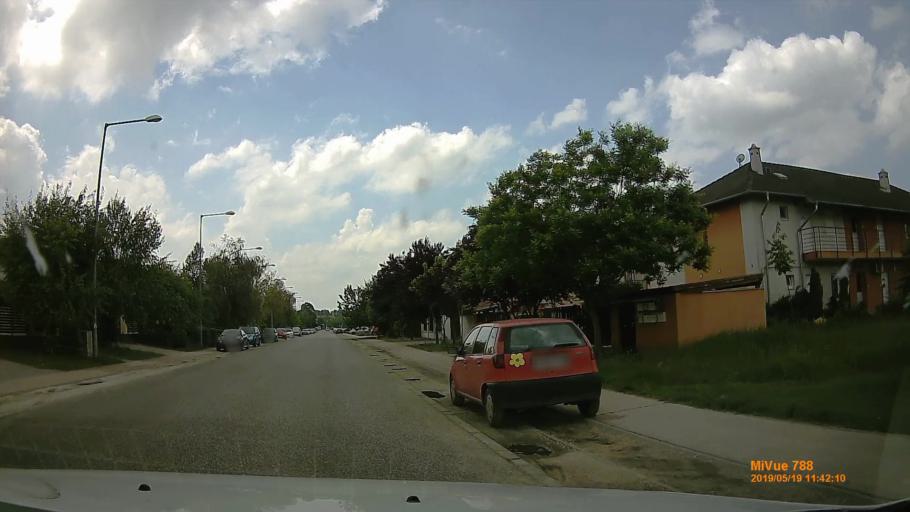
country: HU
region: Budapest
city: Budapest XVII. keruelet
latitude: 47.4721
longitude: 19.2293
